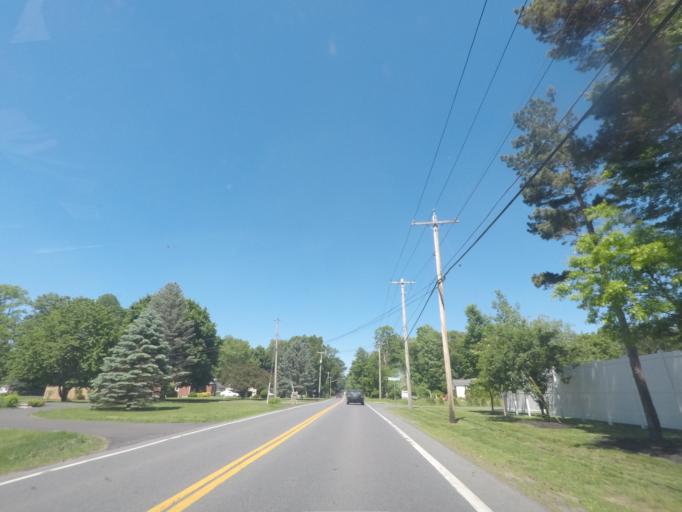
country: US
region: New York
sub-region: Saratoga County
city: Country Knolls
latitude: 42.8558
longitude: -73.7973
